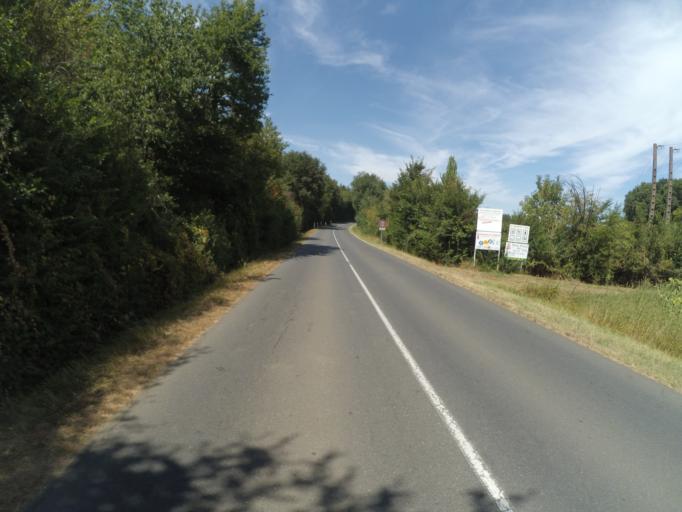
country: FR
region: Poitou-Charentes
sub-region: Departement de la Vienne
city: Usson-du-Poitou
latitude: 46.2128
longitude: 0.5307
